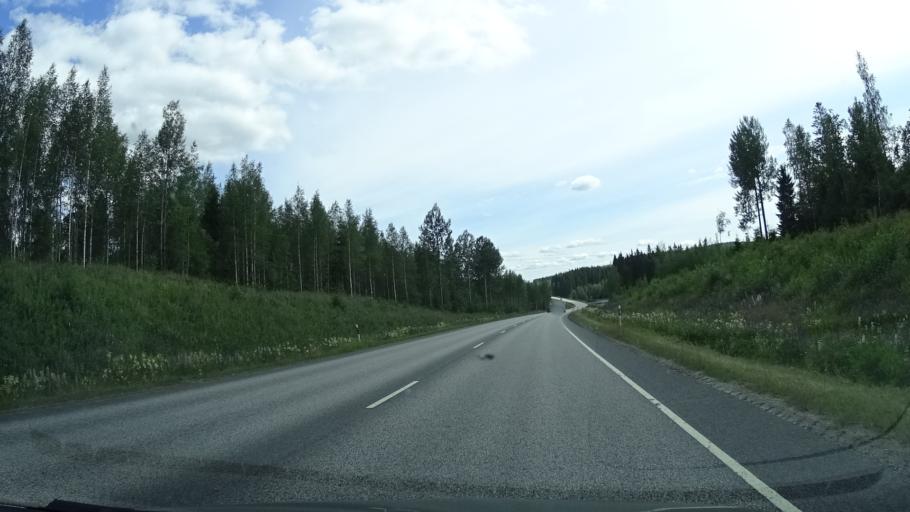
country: FI
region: Central Finland
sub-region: Jyvaeskylae
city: Jyvaeskylae
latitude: 62.2594
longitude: 25.6055
